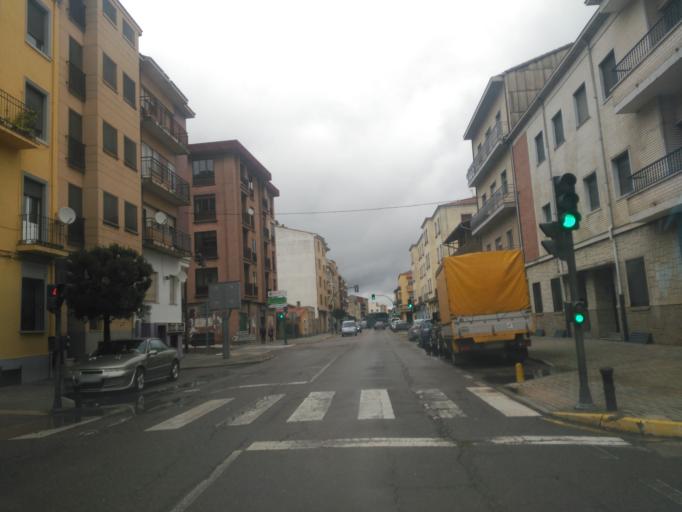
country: ES
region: Castille and Leon
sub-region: Provincia de Salamanca
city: Guijuelo
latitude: 40.5589
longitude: -5.6727
